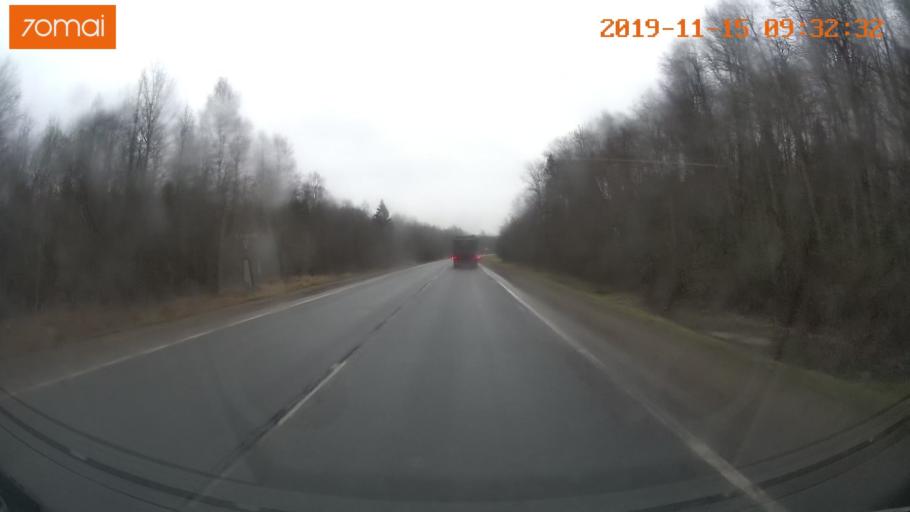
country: RU
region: Vologda
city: Sheksna
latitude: 59.2712
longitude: 38.3377
